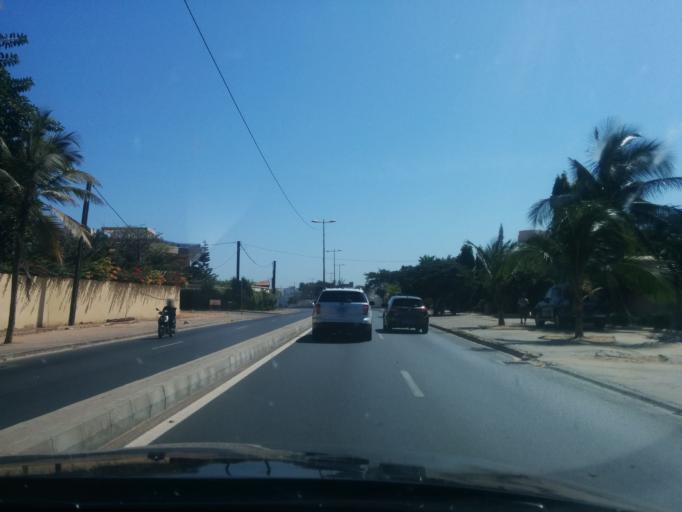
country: SN
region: Dakar
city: Mermoz Boabab
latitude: 14.7029
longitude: -17.4789
